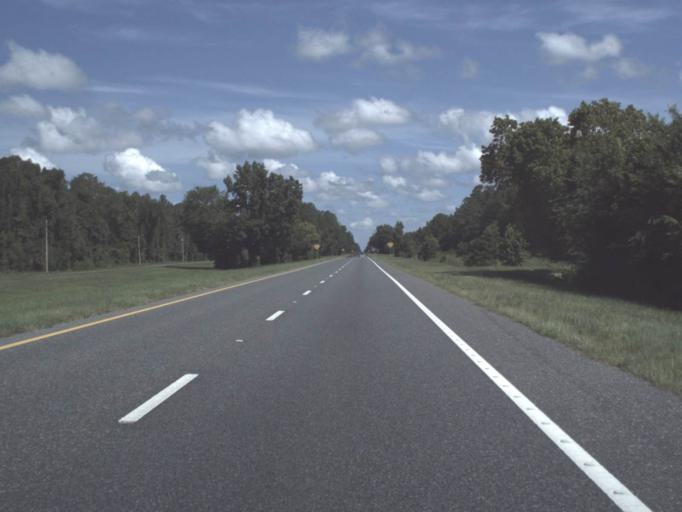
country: US
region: Florida
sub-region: Levy County
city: Williston Highlands
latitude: 29.2466
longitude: -82.7190
